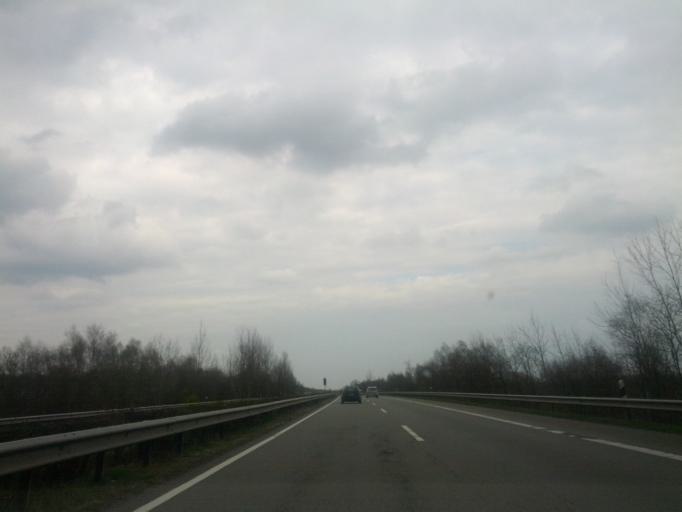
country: DE
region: Lower Saxony
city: Apen
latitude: 53.2801
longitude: 7.8255
